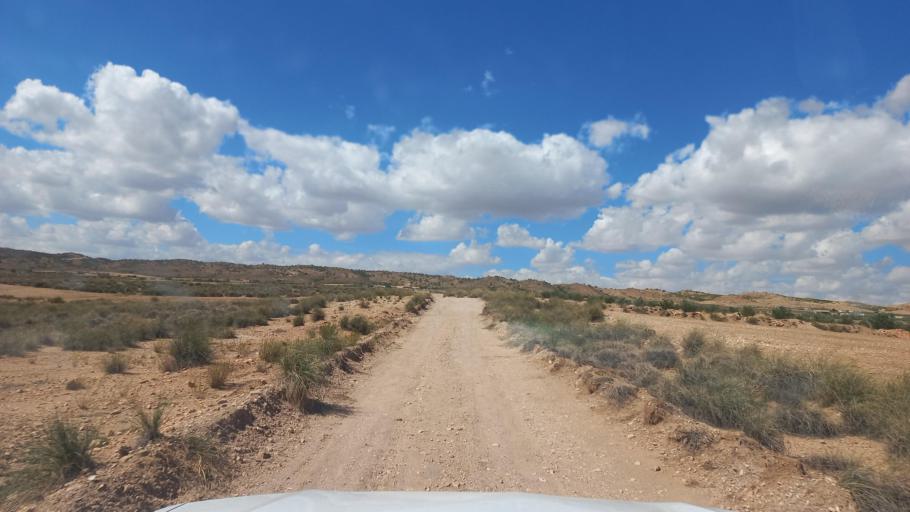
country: TN
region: Al Qasrayn
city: Sbiba
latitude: 35.3591
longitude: 9.0069
